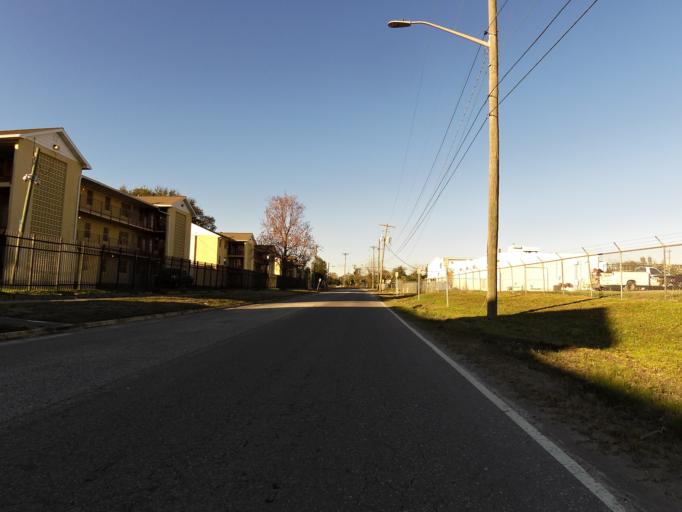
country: US
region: Florida
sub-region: Duval County
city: Jacksonville
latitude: 30.3300
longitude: -81.6967
